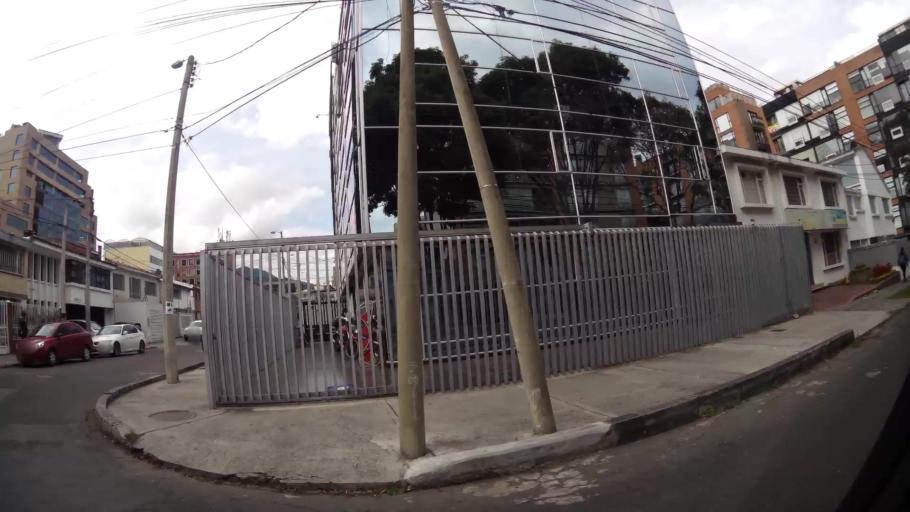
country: CO
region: Bogota D.C.
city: Barrio San Luis
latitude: 4.6999
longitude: -74.0303
